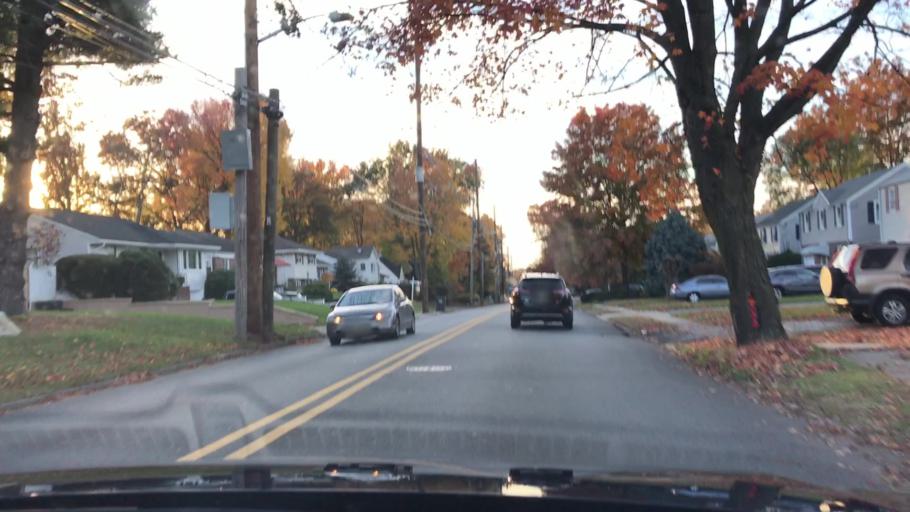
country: US
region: New Jersey
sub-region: Bergen County
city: Teaneck
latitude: 40.9144
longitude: -74.0136
